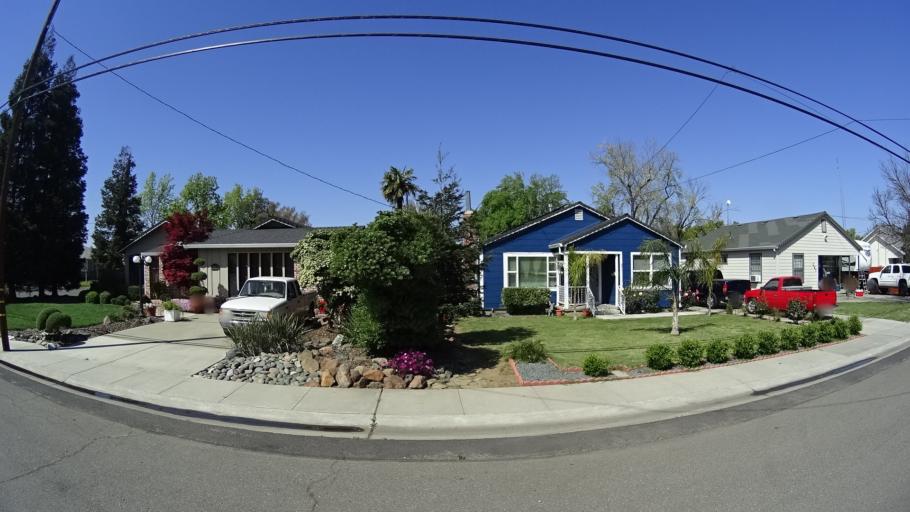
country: US
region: California
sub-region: Glenn County
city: Willows
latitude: 39.5185
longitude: -122.2089
